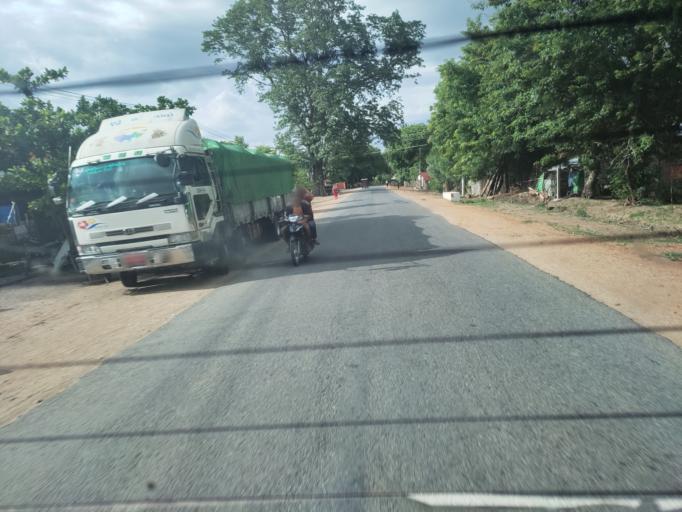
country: MM
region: Magway
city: Magway
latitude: 19.9936
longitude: 94.9884
